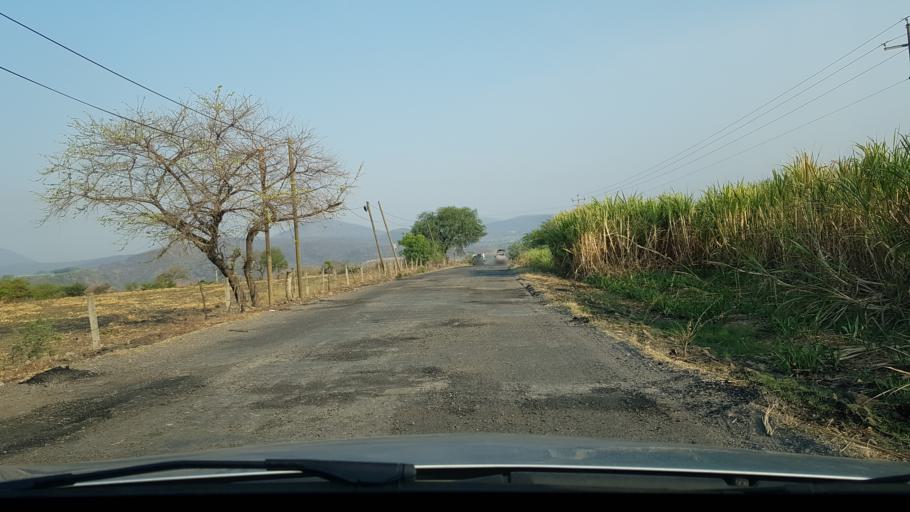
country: MX
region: Morelos
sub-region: Tepalcingo
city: Zacapalco
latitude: 18.6290
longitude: -99.0083
